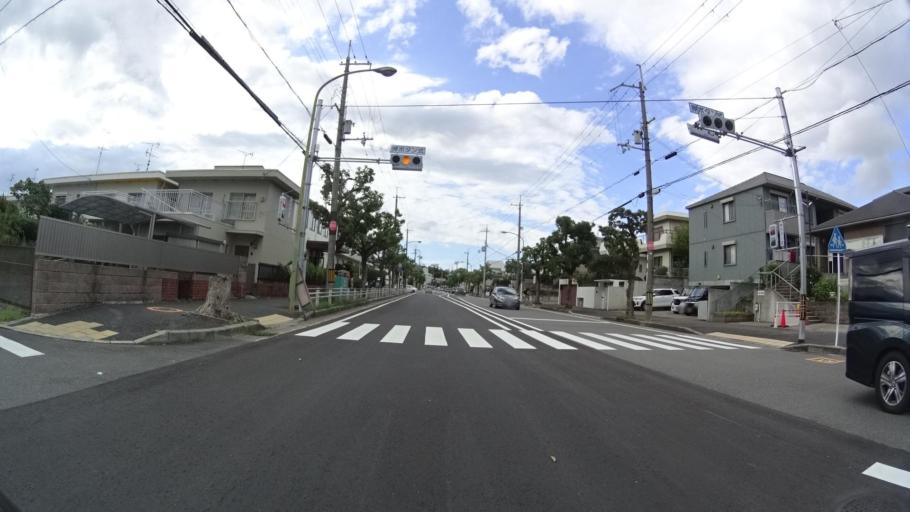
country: JP
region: Kyoto
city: Yawata
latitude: 34.8664
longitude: 135.6926
